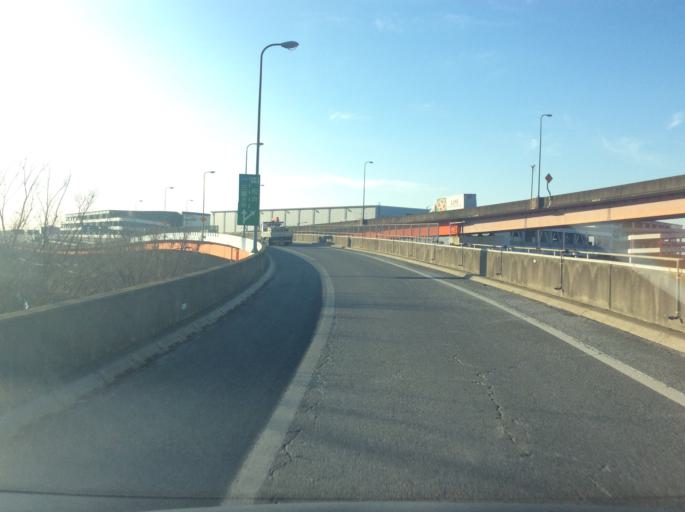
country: JP
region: Saitama
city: Yashio-shi
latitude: 35.8360
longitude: 139.8607
